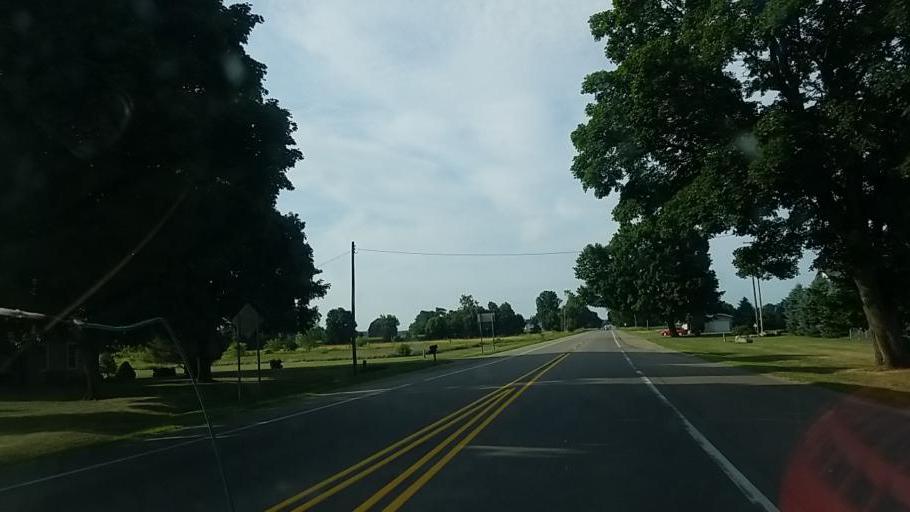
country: US
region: Michigan
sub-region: Ionia County
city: Ionia
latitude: 42.9281
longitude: -85.0748
